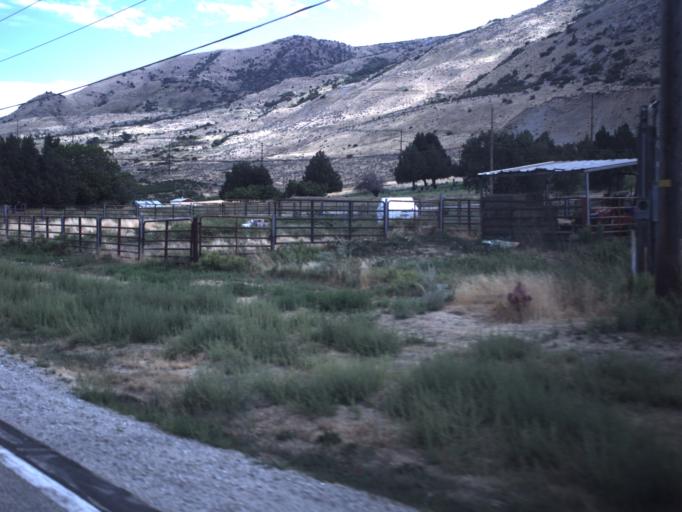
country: US
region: Utah
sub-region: Box Elder County
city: Willard
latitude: 41.4171
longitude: -112.0359
